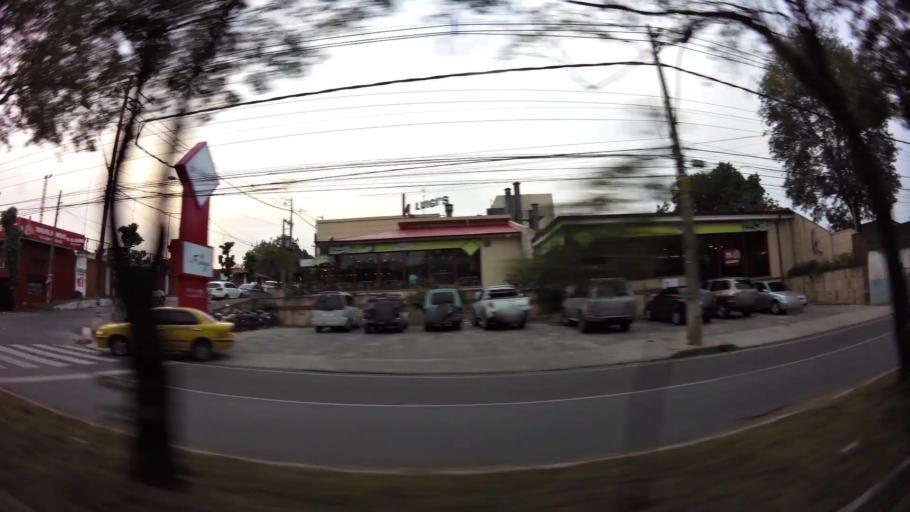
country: PY
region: Asuncion
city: Asuncion
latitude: -25.3137
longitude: -57.6182
